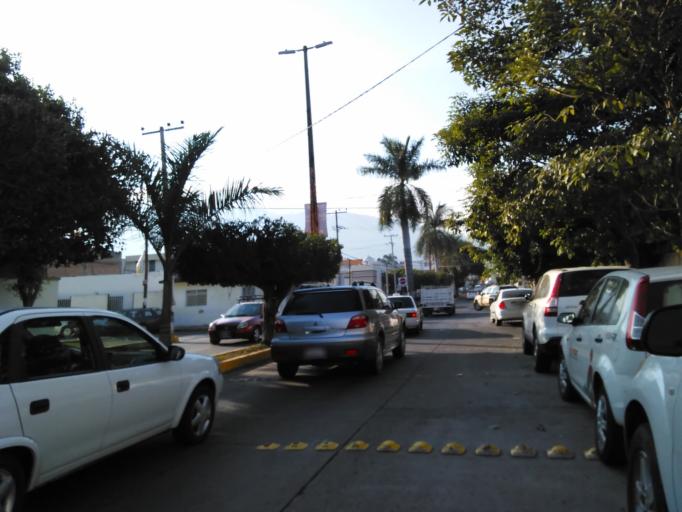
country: MX
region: Nayarit
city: Tepic
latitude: 21.5000
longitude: -104.9004
